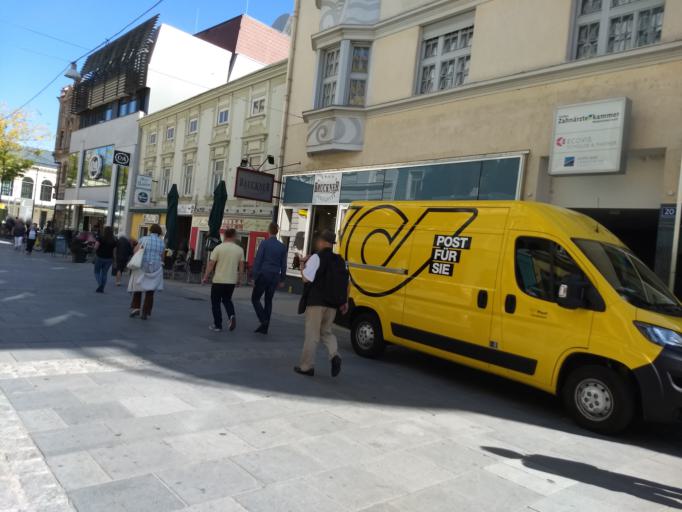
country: AT
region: Lower Austria
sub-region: Sankt Polten Stadt
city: Sankt Poelten
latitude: 48.2069
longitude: 15.6246
